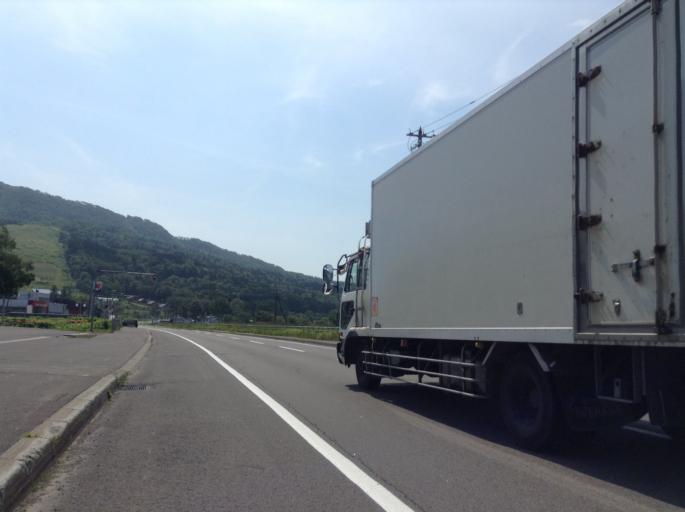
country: JP
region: Hokkaido
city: Nayoro
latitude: 44.7252
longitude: 142.2637
